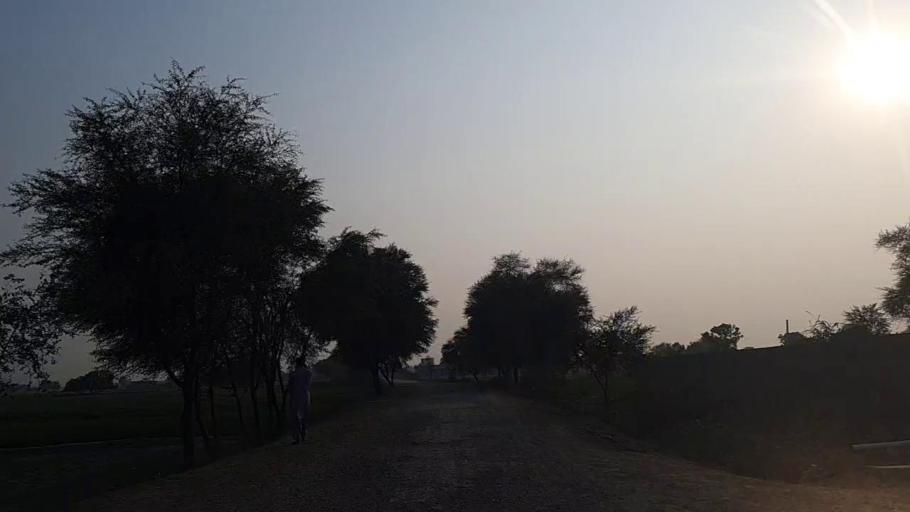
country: PK
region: Sindh
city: Nawabshah
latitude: 26.2178
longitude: 68.4735
